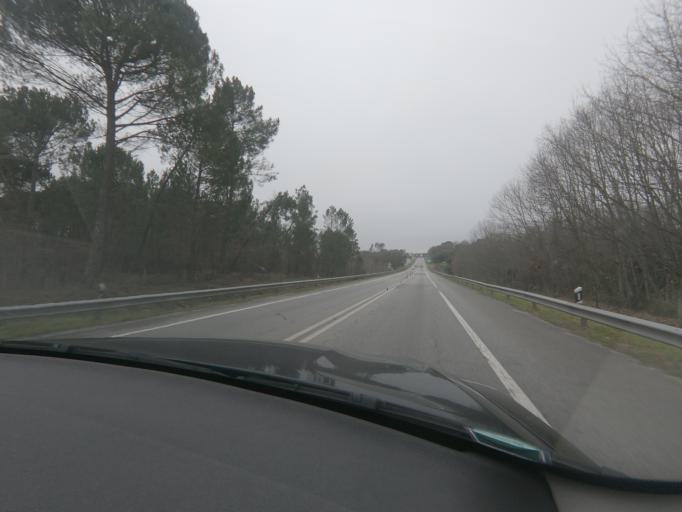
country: PT
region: Viseu
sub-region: Concelho de Tondela
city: Tondela
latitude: 40.5280
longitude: -8.0737
